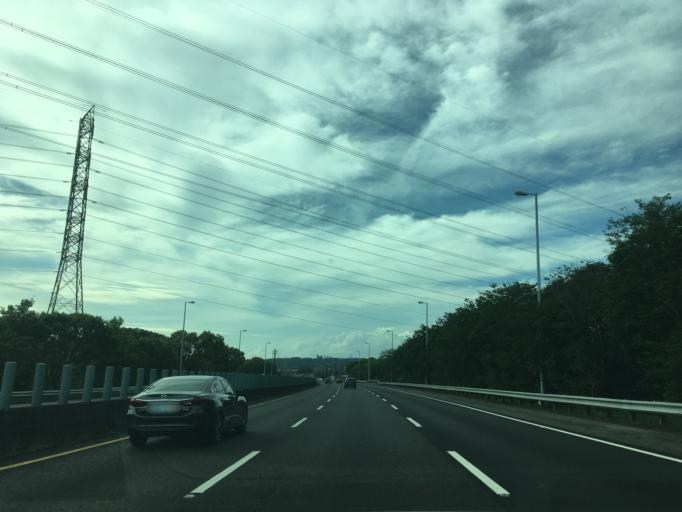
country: TW
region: Taiwan
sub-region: Chiayi
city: Jiayi Shi
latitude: 23.5018
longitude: 120.4922
